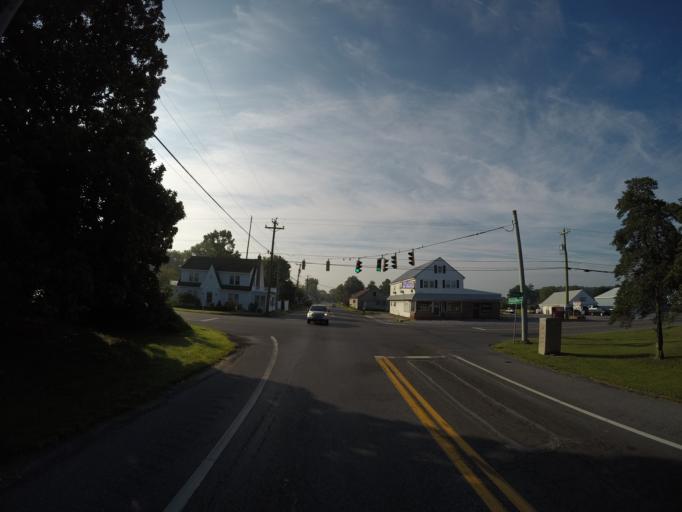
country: US
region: Delaware
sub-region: Sussex County
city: Selbyville
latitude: 38.4967
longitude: -75.1710
